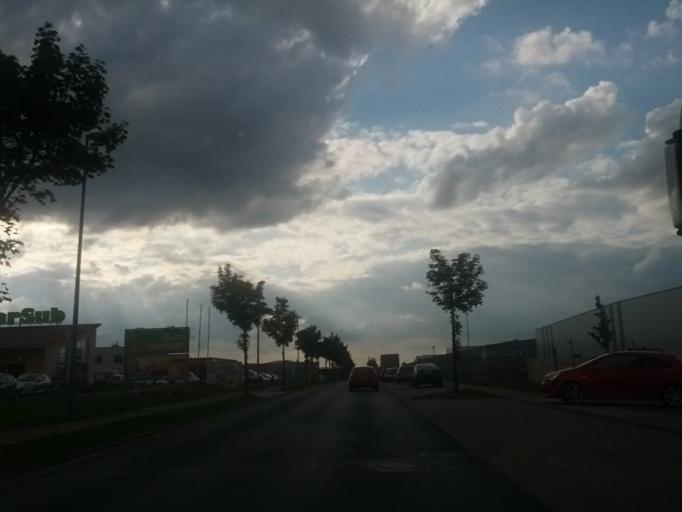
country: DE
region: Thuringia
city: Emleben
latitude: 50.9201
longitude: 10.7196
